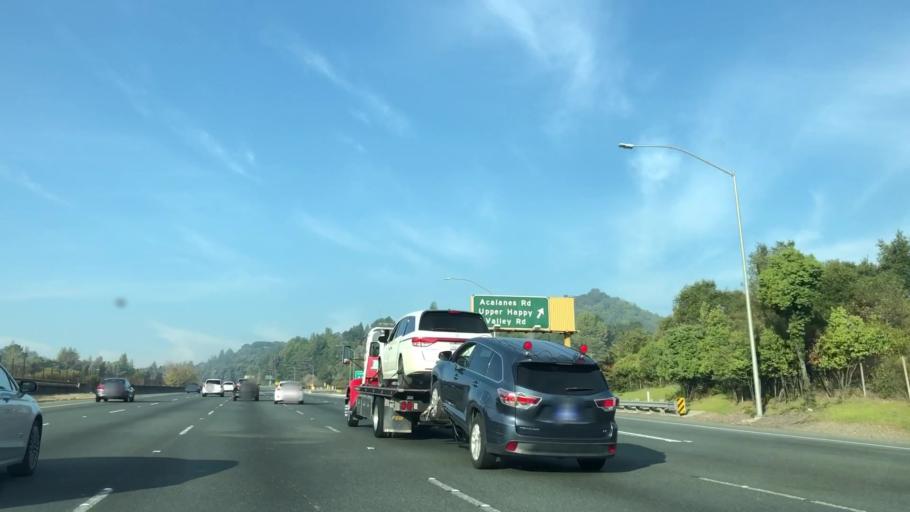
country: US
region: California
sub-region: Contra Costa County
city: Orinda
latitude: 37.8928
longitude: -122.1512
